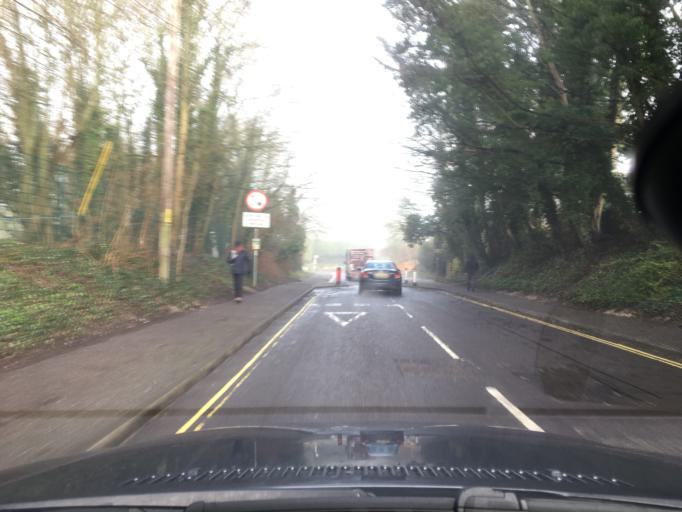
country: GB
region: England
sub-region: Hampshire
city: Old Basing
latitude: 51.2694
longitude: -1.0448
